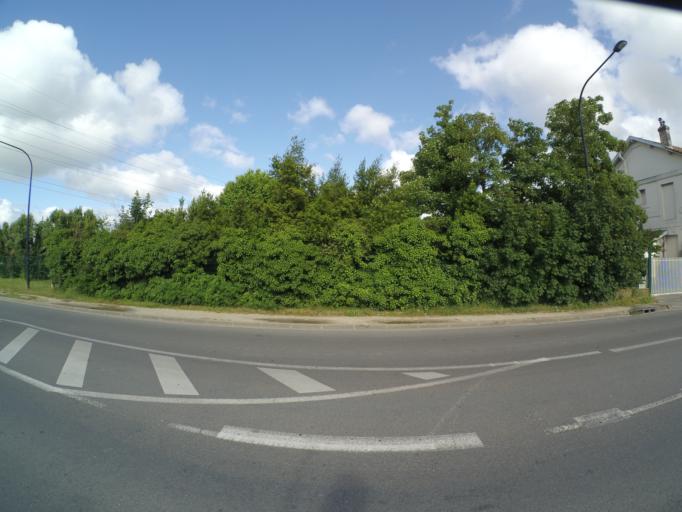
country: FR
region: Aquitaine
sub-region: Departement de la Gironde
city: Lormont
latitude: 44.8849
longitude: -0.5499
